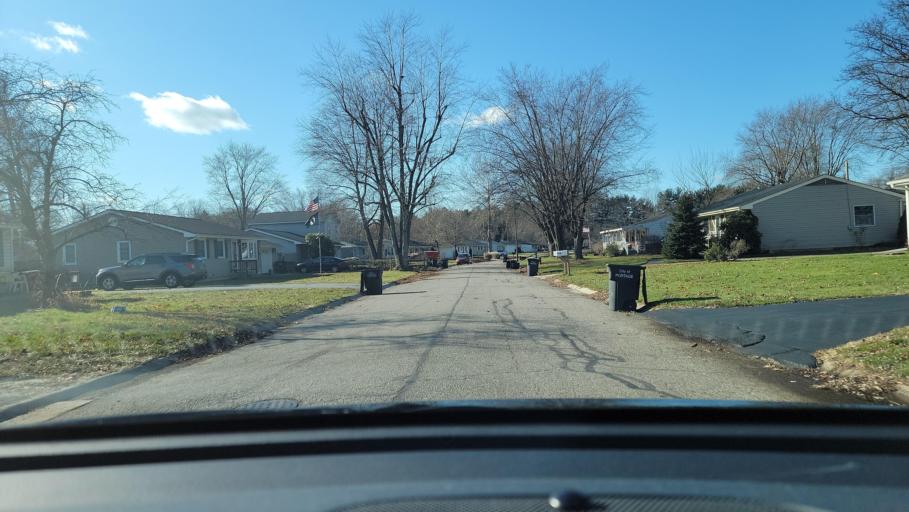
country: US
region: Indiana
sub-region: Porter County
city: Portage
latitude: 41.5843
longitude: -87.1905
